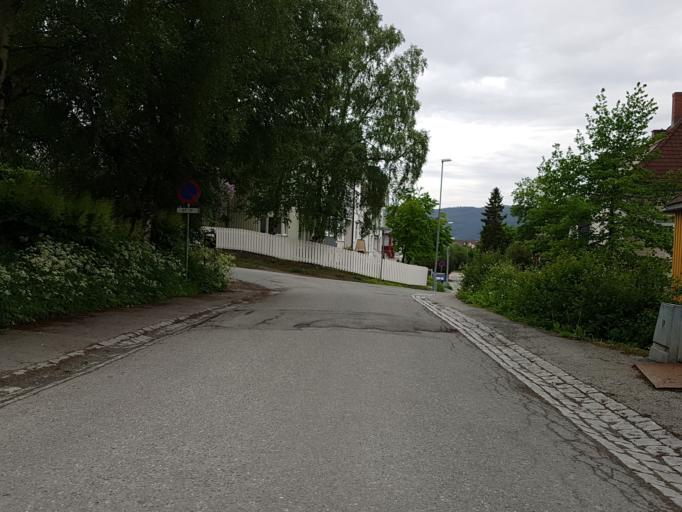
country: NO
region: Sor-Trondelag
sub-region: Trondheim
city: Trondheim
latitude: 63.4364
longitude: 10.4358
